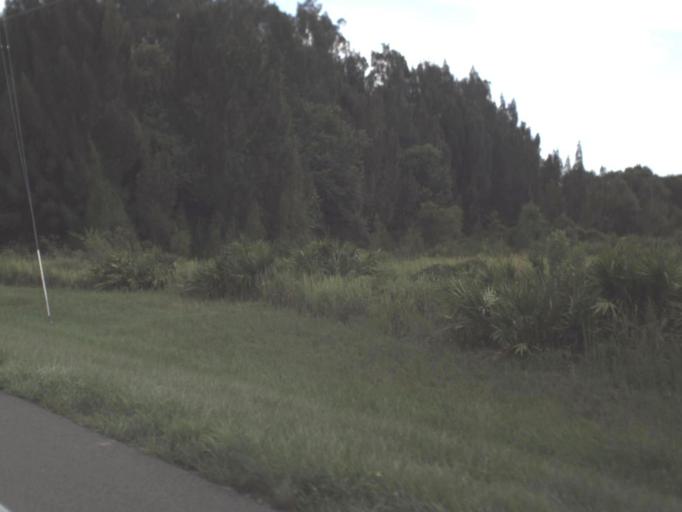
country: US
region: Florida
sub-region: DeSoto County
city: Nocatee
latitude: 27.1768
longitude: -81.8736
